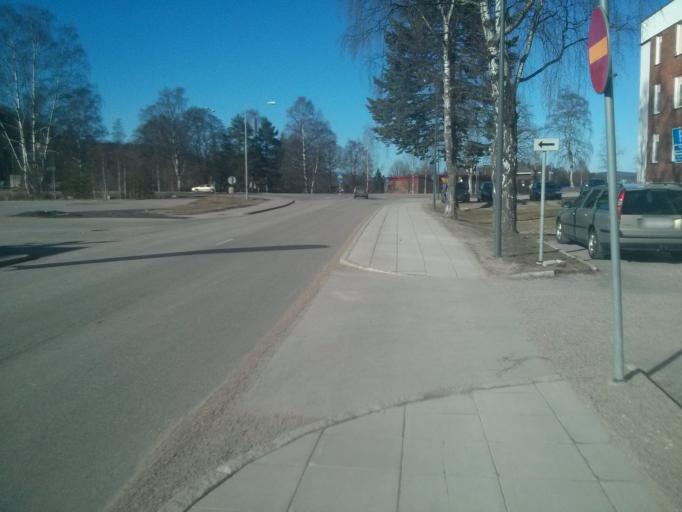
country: SE
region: Vaesternorrland
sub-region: Sundsvalls Kommun
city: Kvissleby
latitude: 62.3017
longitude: 17.3779
